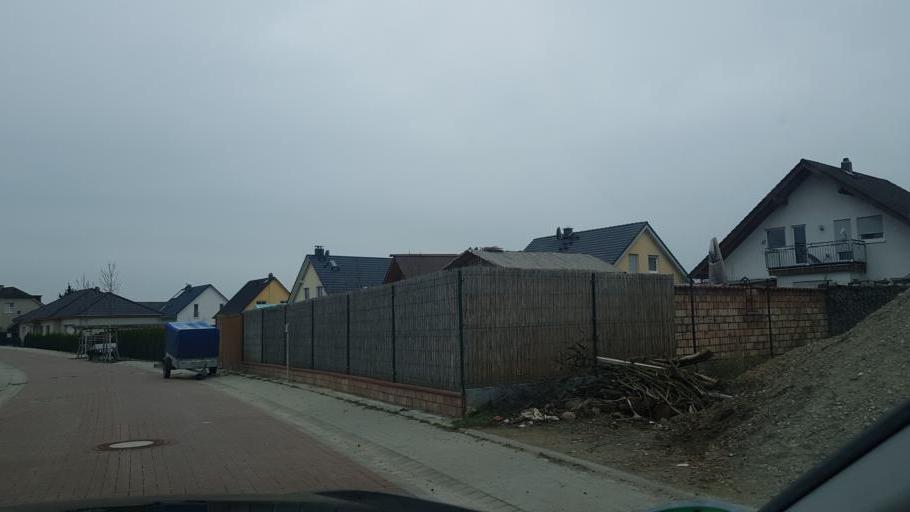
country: DE
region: Brandenburg
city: Mittenwalde
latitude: 52.2907
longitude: 13.5369
